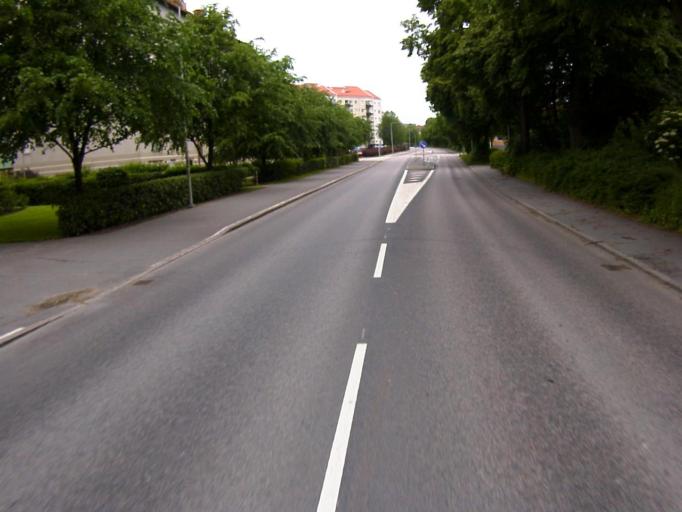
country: SE
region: Skane
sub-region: Kristianstads Kommun
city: Kristianstad
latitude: 56.0355
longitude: 14.1647
